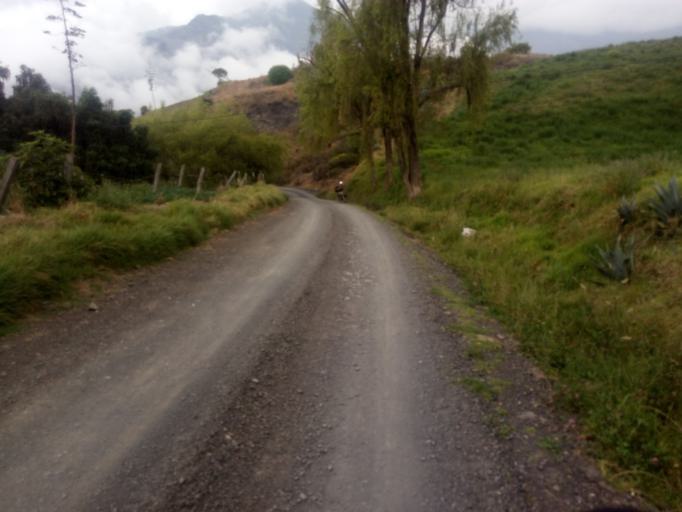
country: CO
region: Boyaca
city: Chita
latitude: 6.1932
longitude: -72.4858
